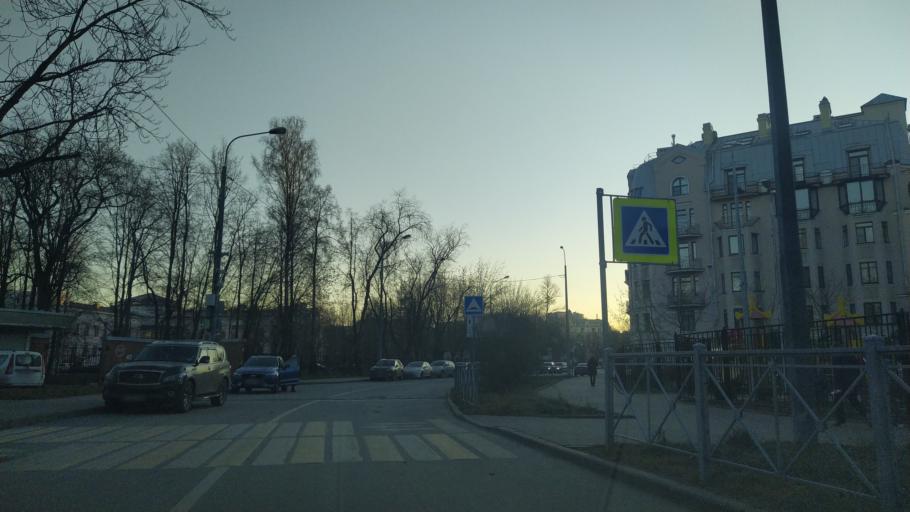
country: RU
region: Leningrad
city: Krestovskiy ostrov
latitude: 59.9725
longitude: 30.2761
